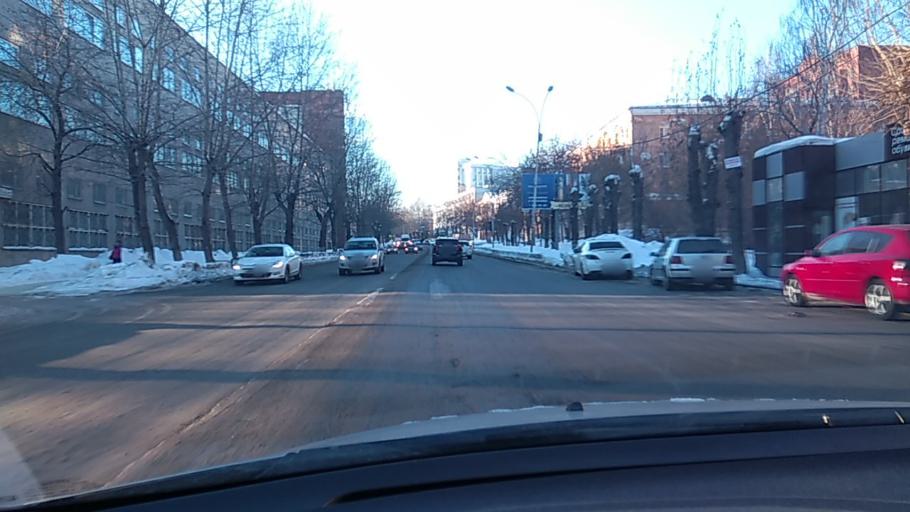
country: RU
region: Sverdlovsk
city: Yekaterinburg
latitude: 56.8251
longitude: 60.6449
